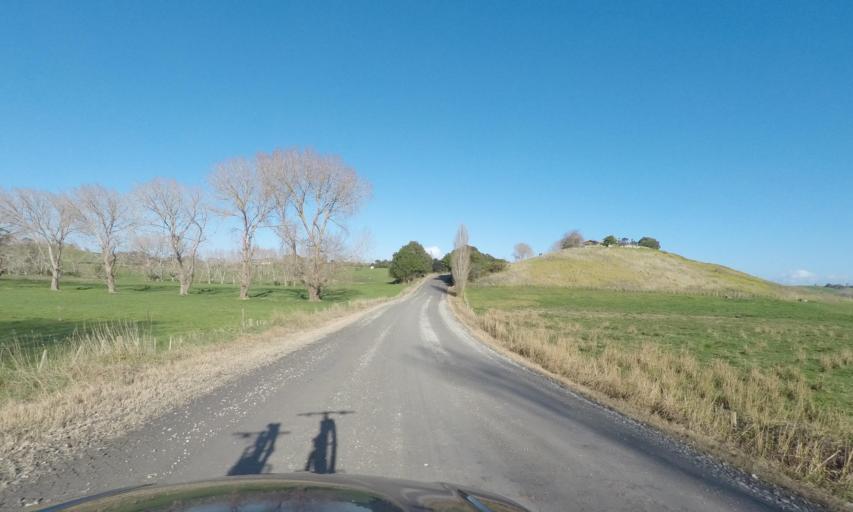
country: NZ
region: Auckland
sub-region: Auckland
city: Wellsford
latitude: -36.1512
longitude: 174.6060
